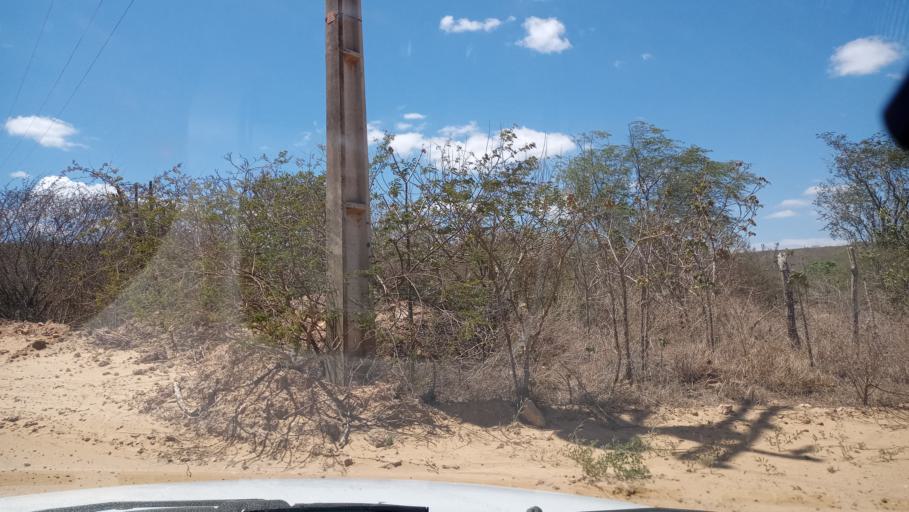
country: BR
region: Rio Grande do Norte
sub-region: Sao Paulo Do Potengi
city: Sao Paulo do Potengi
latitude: -5.7717
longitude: -35.9113
